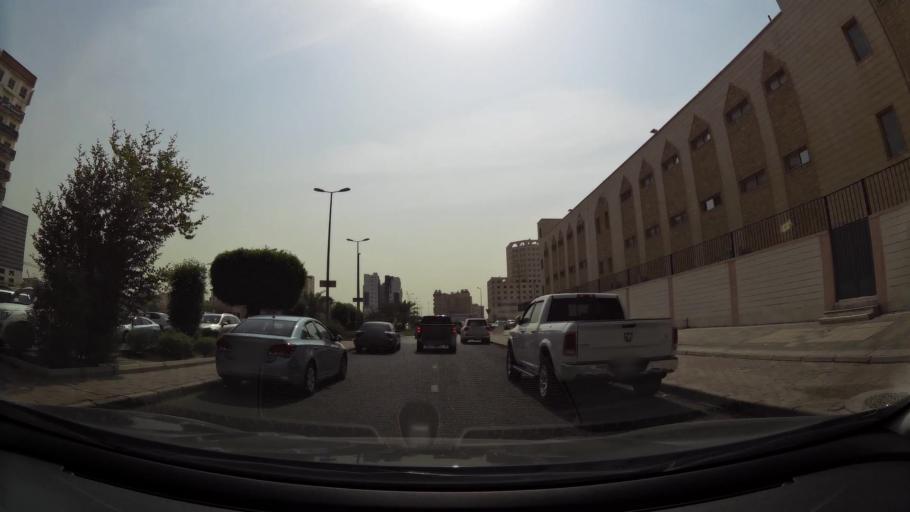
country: KW
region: Al Asimah
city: Ar Rabiyah
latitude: 29.3052
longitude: 47.9090
